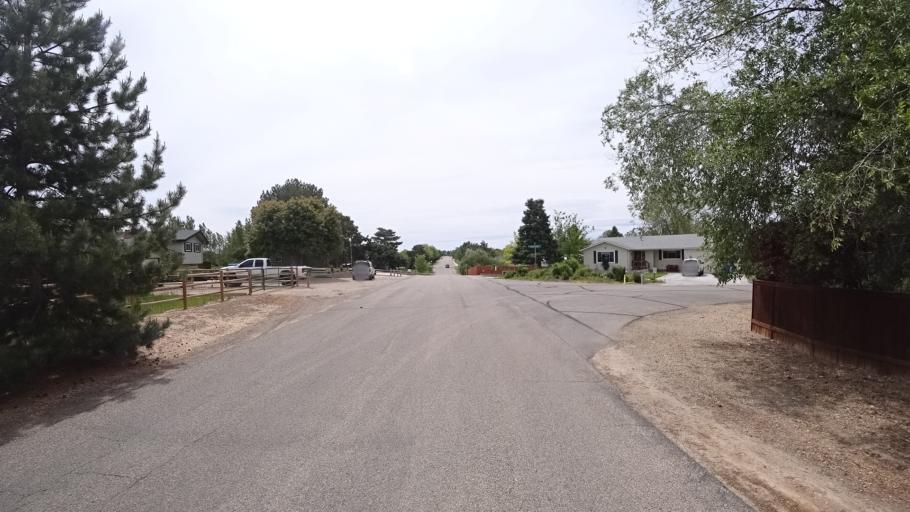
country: US
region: Idaho
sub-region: Ada County
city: Meridian
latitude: 43.5556
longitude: -116.3244
